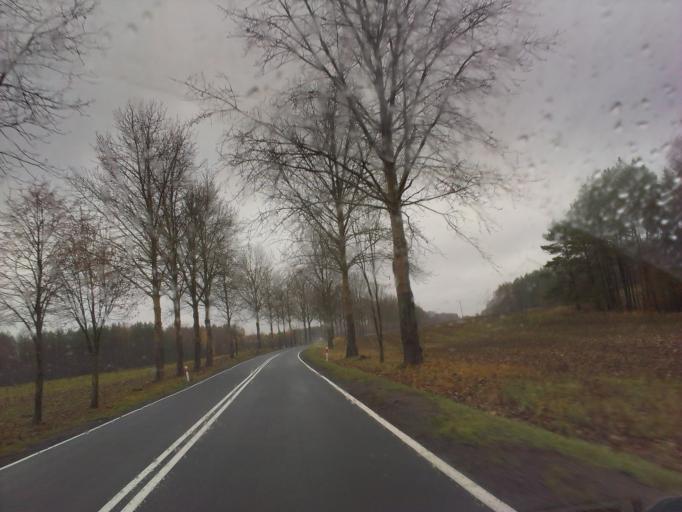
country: PL
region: West Pomeranian Voivodeship
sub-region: Powiat szczecinecki
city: Borne Sulinowo
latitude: 53.6113
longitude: 16.5847
